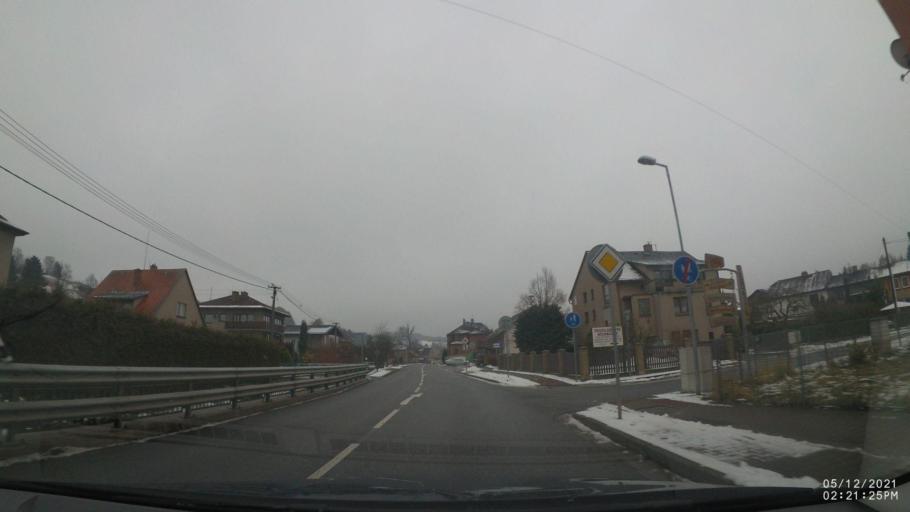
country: CZ
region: Kralovehradecky
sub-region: Okres Nachod
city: Nachod
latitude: 50.4380
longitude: 16.1520
